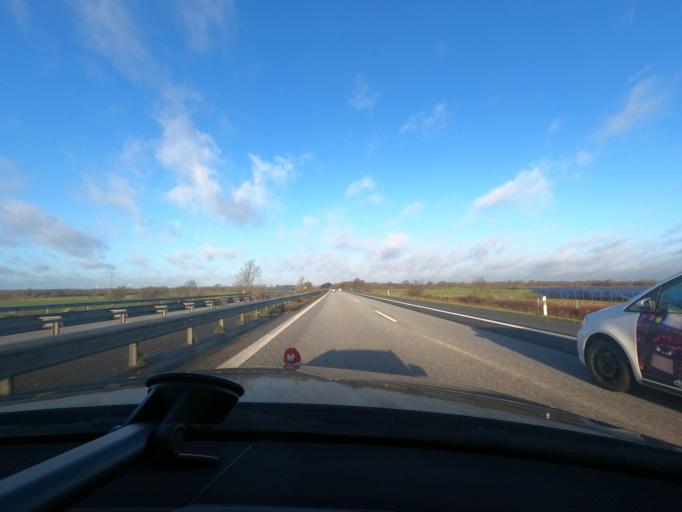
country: DE
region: Schleswig-Holstein
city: Lurschau
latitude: 54.5636
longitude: 9.4686
